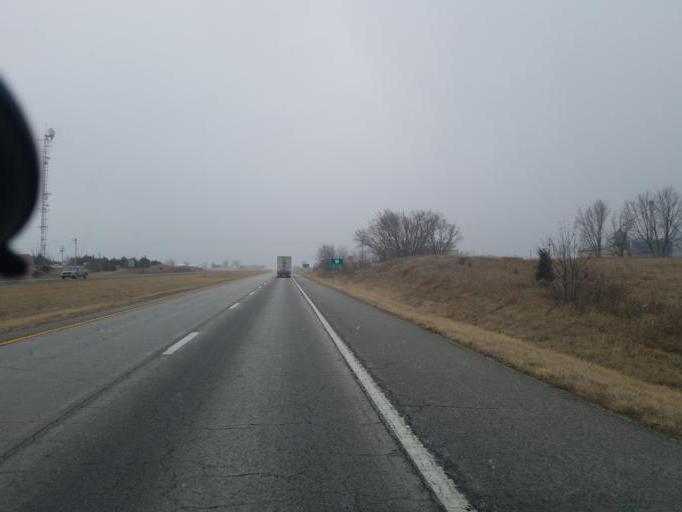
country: US
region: Missouri
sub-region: Macon County
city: La Plata
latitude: 39.9219
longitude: -92.4751
